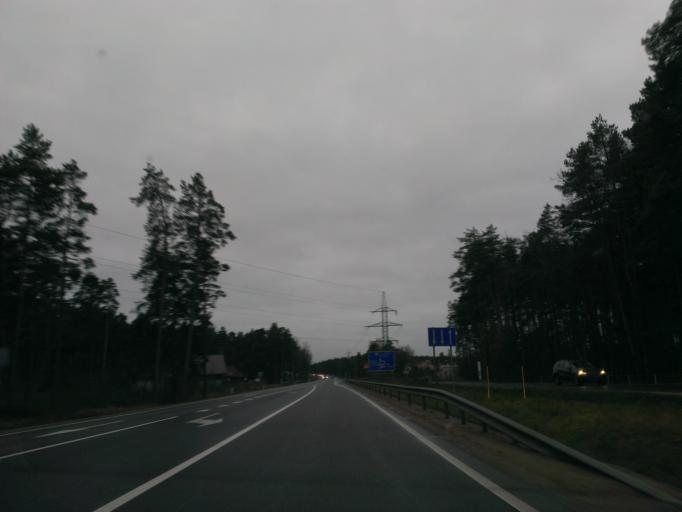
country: LV
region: Riga
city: Bergi
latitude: 57.0210
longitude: 24.3146
